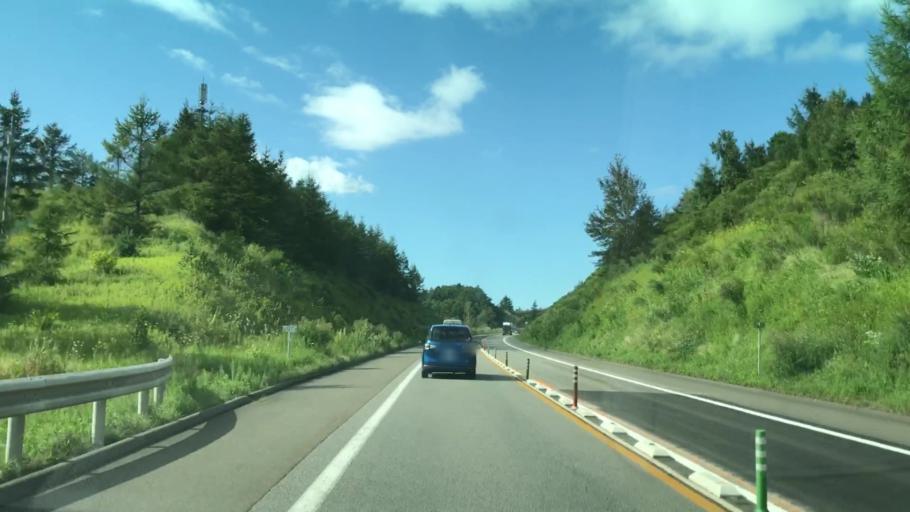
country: JP
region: Hokkaido
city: Date
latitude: 42.4417
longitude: 140.9169
